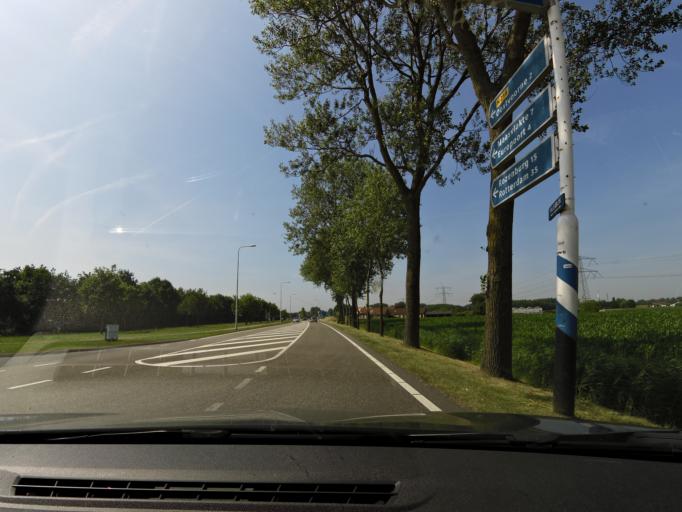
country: NL
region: South Holland
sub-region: Gemeente Brielle
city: Brielle
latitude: 51.9120
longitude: 4.1218
